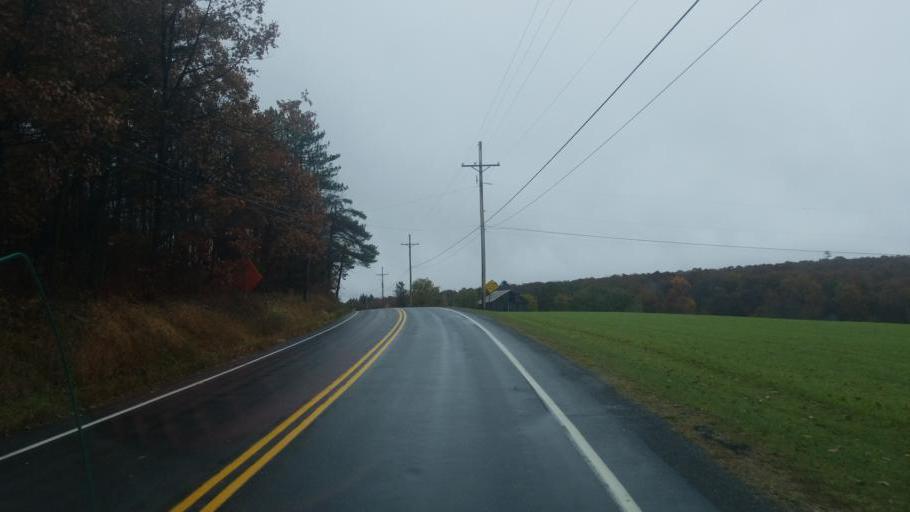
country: US
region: Pennsylvania
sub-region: Centre County
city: Milesburg
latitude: 41.0285
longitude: -77.9677
